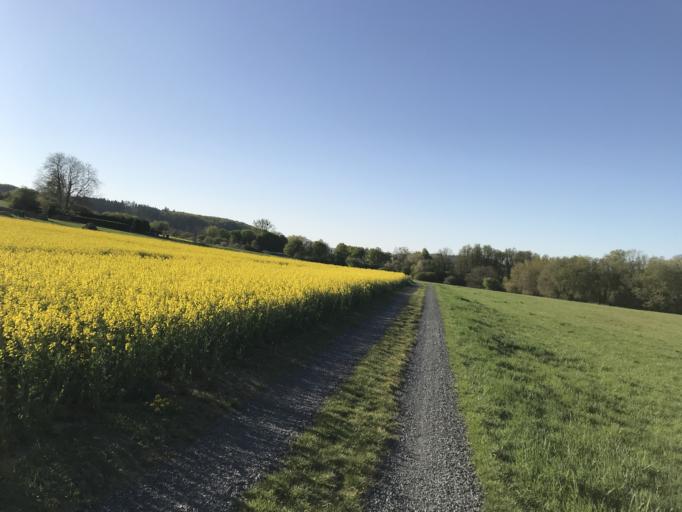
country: DE
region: Hesse
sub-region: Regierungsbezirk Giessen
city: Grossen Buseck
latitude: 50.5913
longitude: 8.8074
